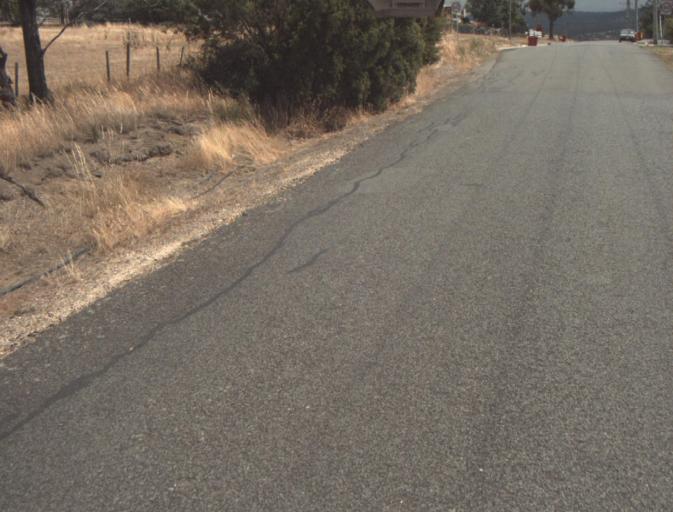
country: AU
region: Tasmania
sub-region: Launceston
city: Newstead
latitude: -41.4504
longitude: 147.2068
